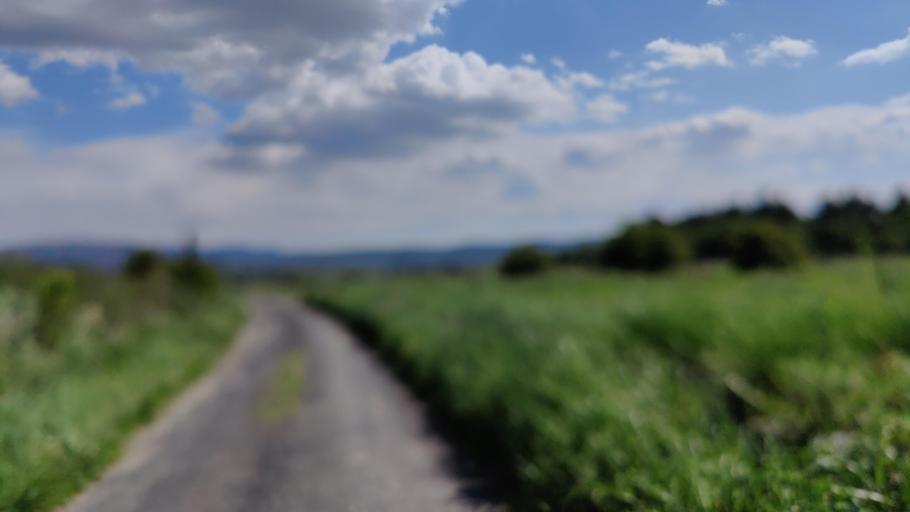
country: FR
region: Languedoc-Roussillon
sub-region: Departement des Pyrenees-Orientales
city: Estagel
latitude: 42.8849
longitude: 2.7198
